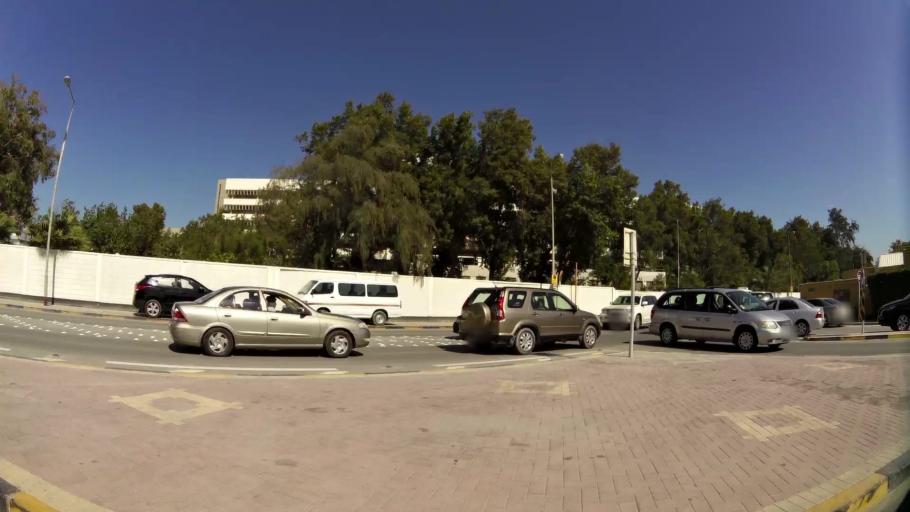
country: BH
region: Manama
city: Manama
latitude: 26.2157
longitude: 50.5701
